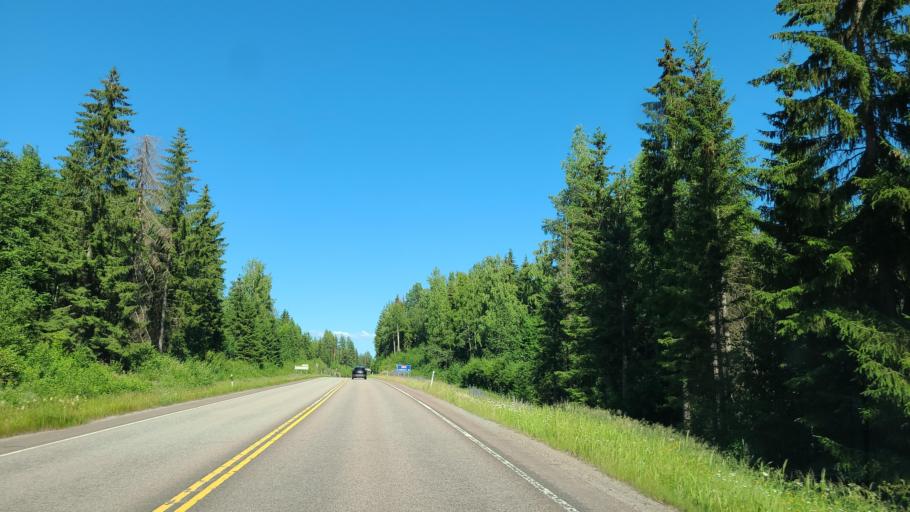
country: FI
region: Central Finland
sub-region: Jyvaeskylae
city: Petaejaevesi
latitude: 62.2713
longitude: 25.3444
